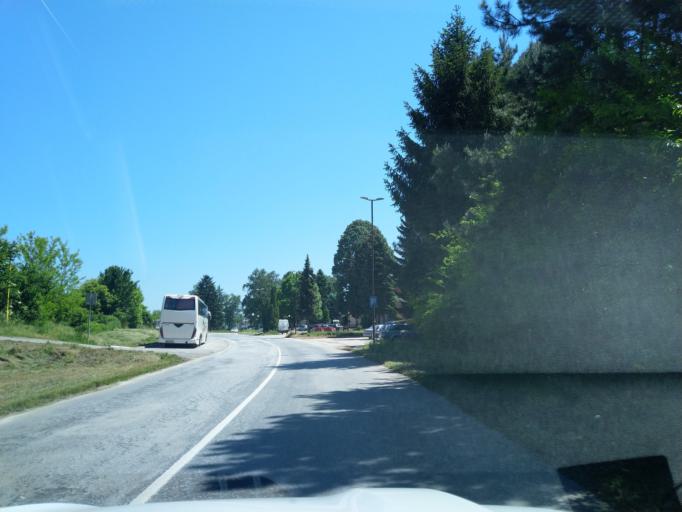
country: RS
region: Central Serbia
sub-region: Zlatiborski Okrug
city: Pozega
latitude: 43.8418
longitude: 20.0280
